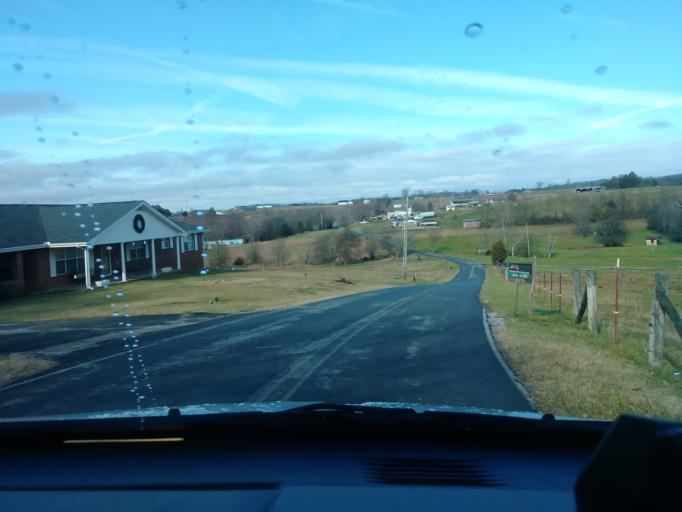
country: US
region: Tennessee
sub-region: Greene County
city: Mosheim
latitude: 36.0899
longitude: -82.9136
